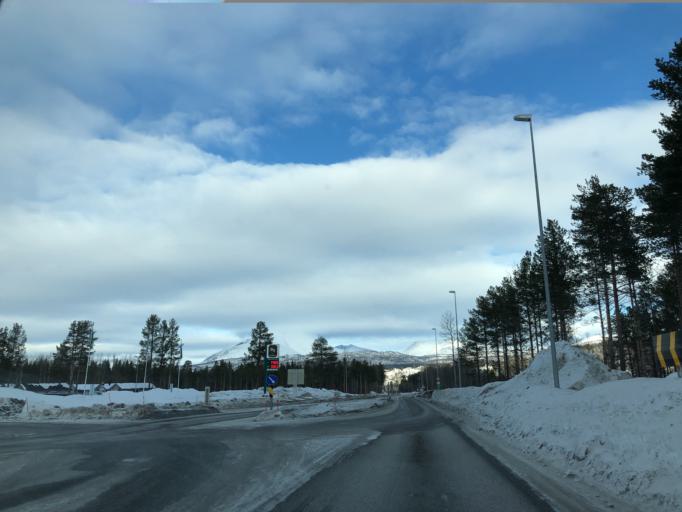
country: NO
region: Troms
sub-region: Malselv
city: Moen
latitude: 69.1324
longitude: 18.5805
